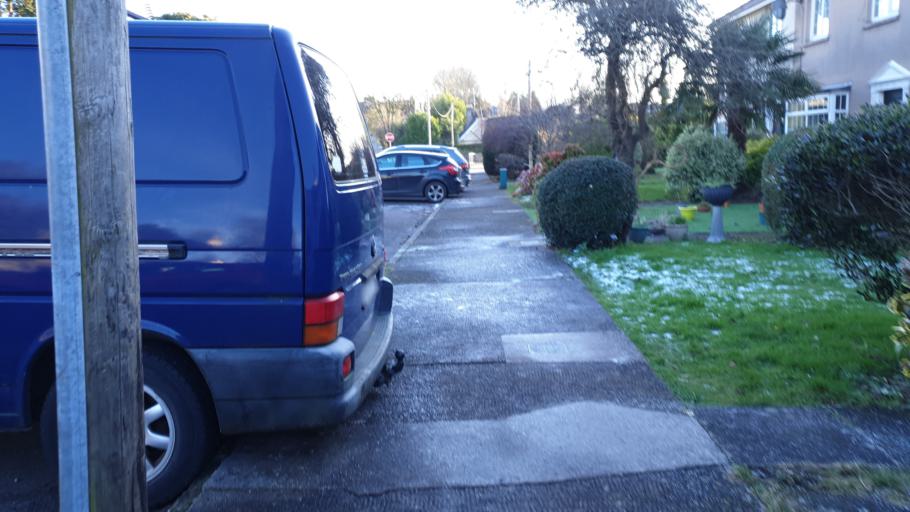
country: IE
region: Munster
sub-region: County Cork
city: Cork
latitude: 51.8927
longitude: -8.4395
